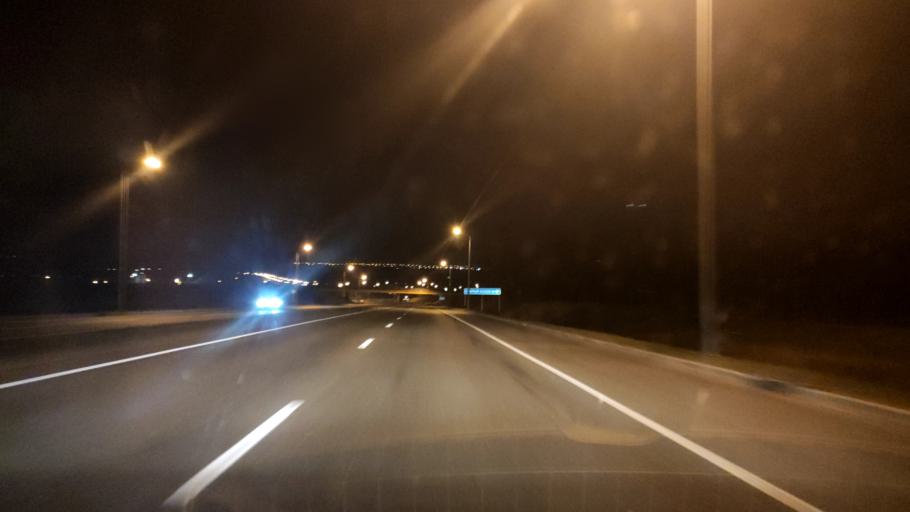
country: RU
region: Belgorod
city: Staryy Oskol
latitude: 51.3396
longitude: 37.7902
